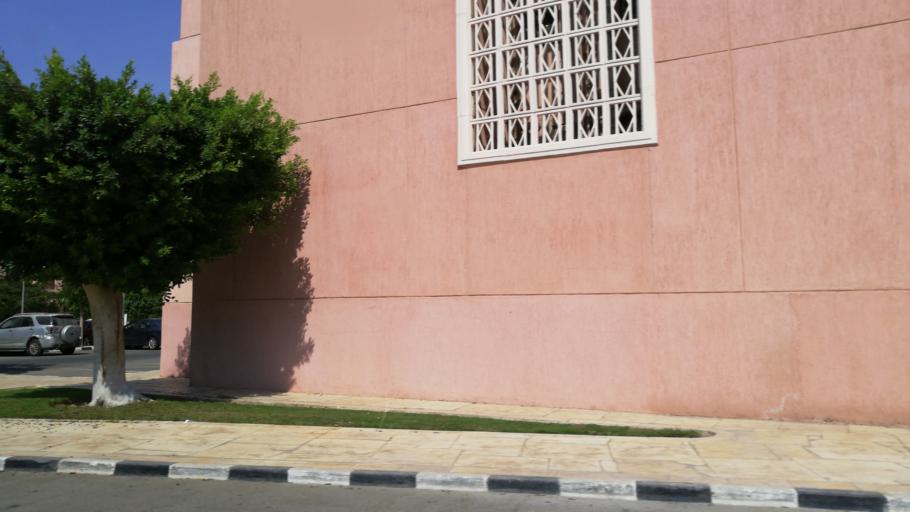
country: EG
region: Muhafazat al Qalyubiyah
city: Al Khankah
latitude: 30.0625
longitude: 31.4878
